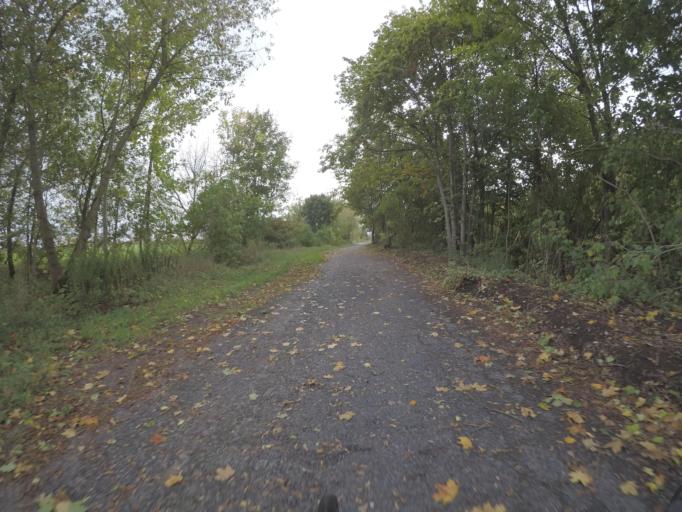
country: DE
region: Berlin
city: Blankenfelde
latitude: 52.6646
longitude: 13.3894
